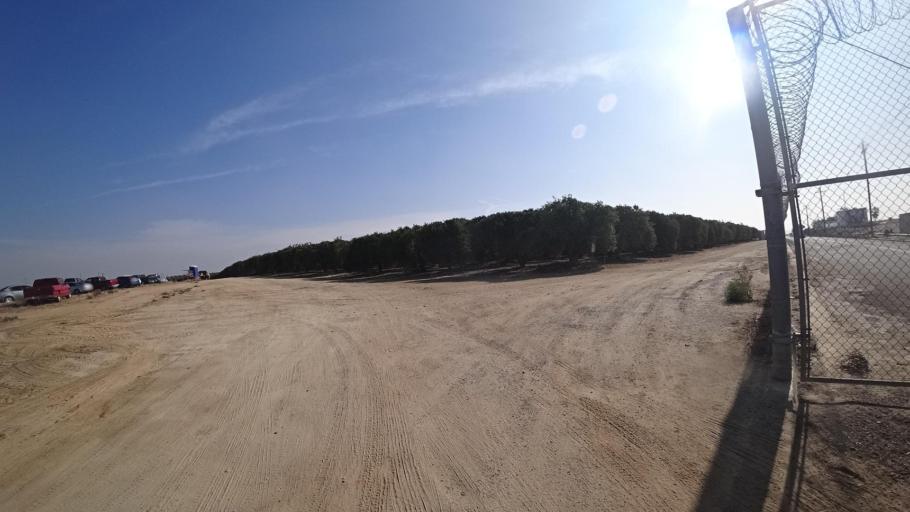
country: US
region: California
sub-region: Kern County
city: Oildale
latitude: 35.5141
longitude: -119.1086
